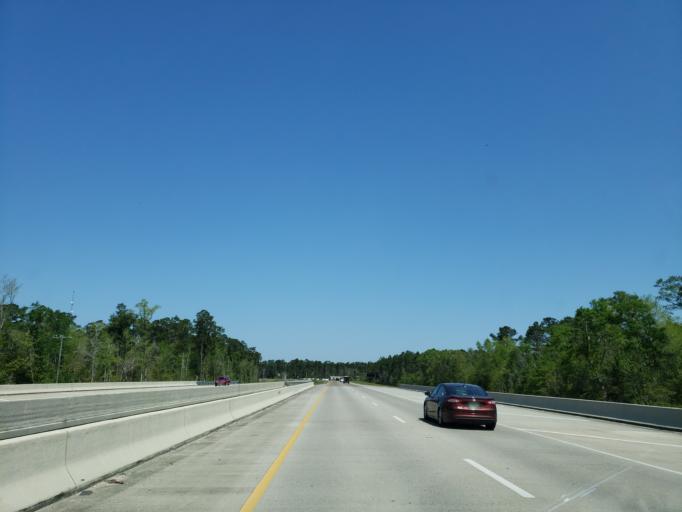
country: US
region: Mississippi
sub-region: Harrison County
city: Lyman
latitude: 30.5225
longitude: -89.1085
